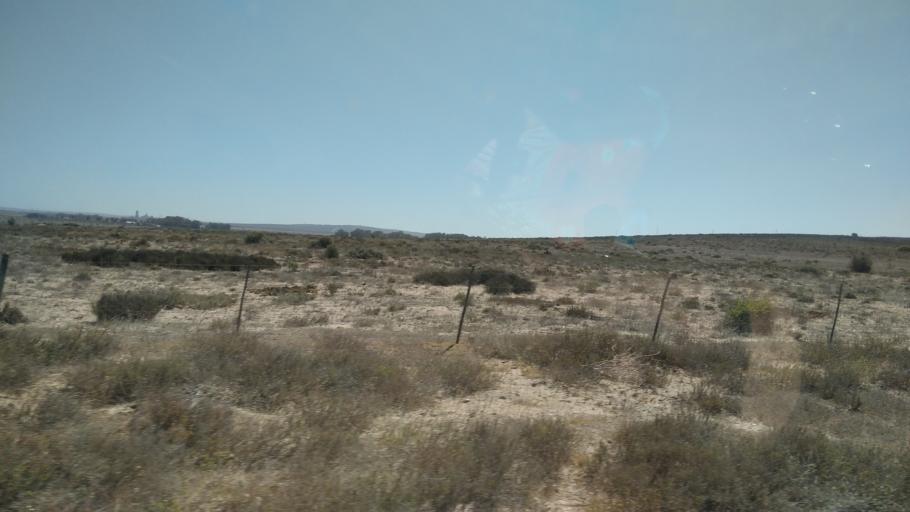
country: ZA
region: Western Cape
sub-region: West Coast District Municipality
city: Vredenburg
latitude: -33.0134
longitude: 18.1158
